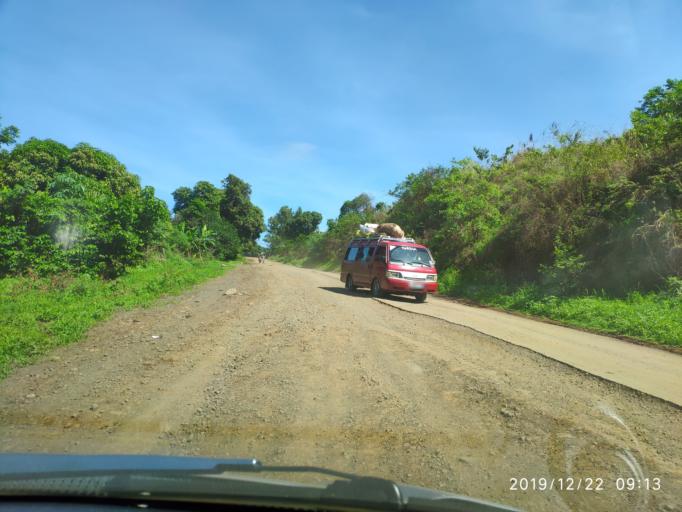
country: MG
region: Diana
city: Sadjoavato
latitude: -12.7572
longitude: 49.2384
